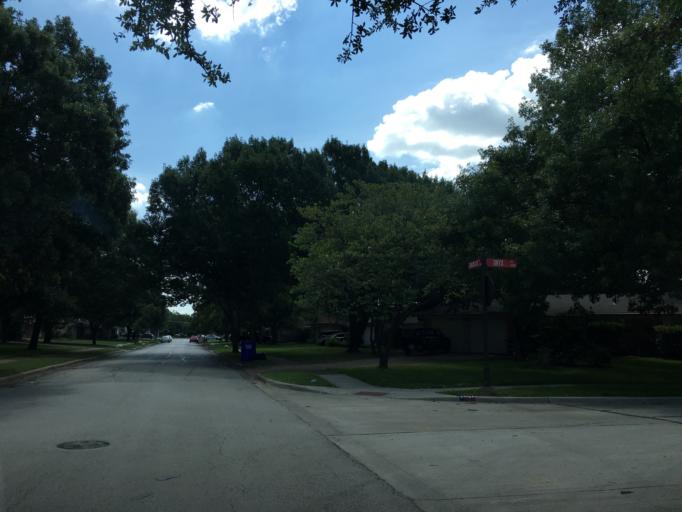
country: US
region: Texas
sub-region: Dallas County
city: Farmers Branch
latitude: 32.9313
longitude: -96.8755
